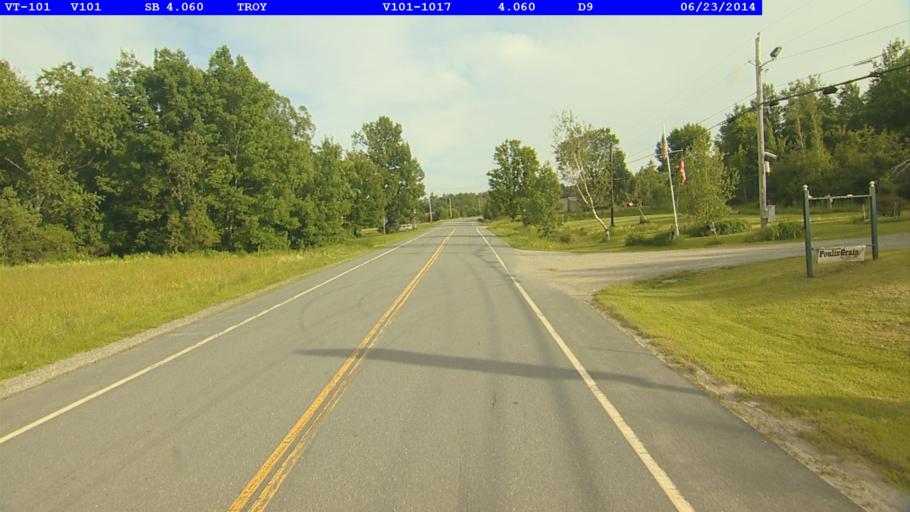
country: US
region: Vermont
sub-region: Orleans County
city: Newport
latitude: 44.9608
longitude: -72.4133
